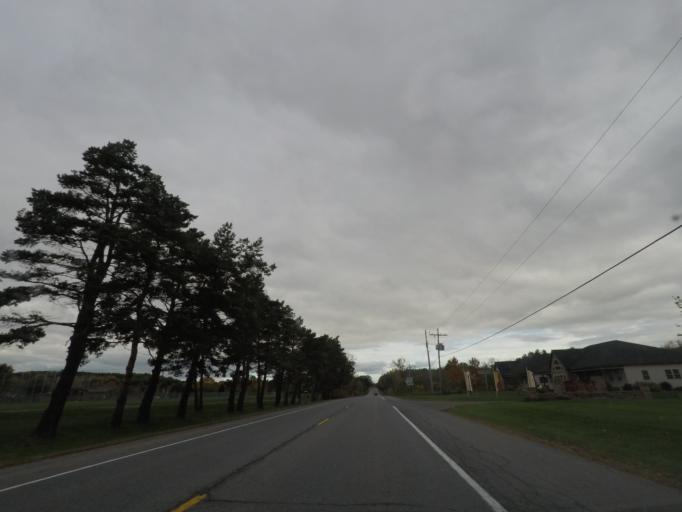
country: US
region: New York
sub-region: Saratoga County
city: Mechanicville
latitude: 42.8620
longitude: -73.7265
